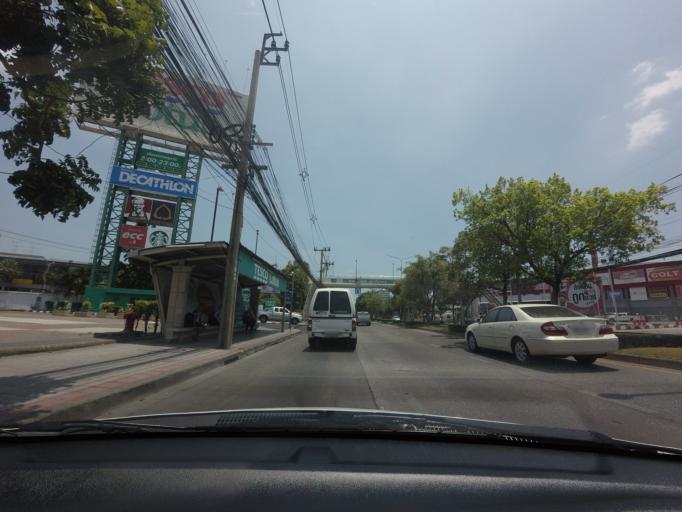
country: TH
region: Bangkok
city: Khan Na Yao
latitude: 13.8243
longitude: 100.6564
